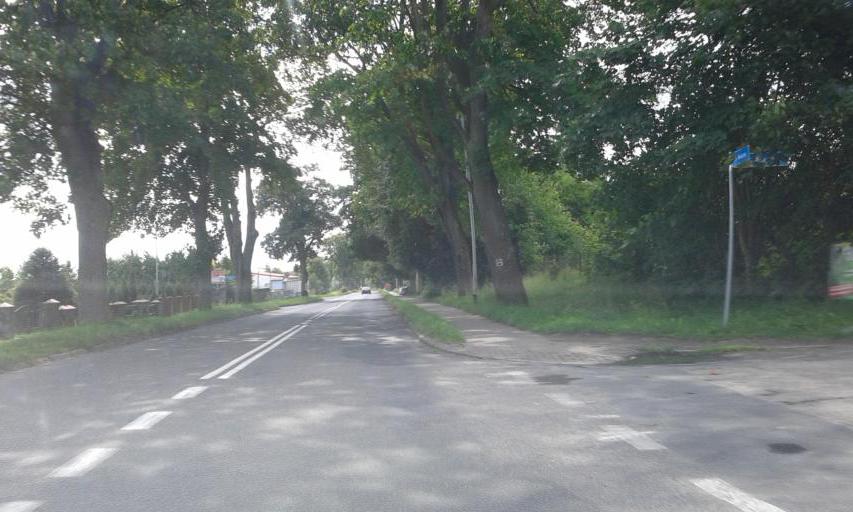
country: PL
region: West Pomeranian Voivodeship
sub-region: Powiat drawski
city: Czaplinek
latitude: 53.5497
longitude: 16.2420
